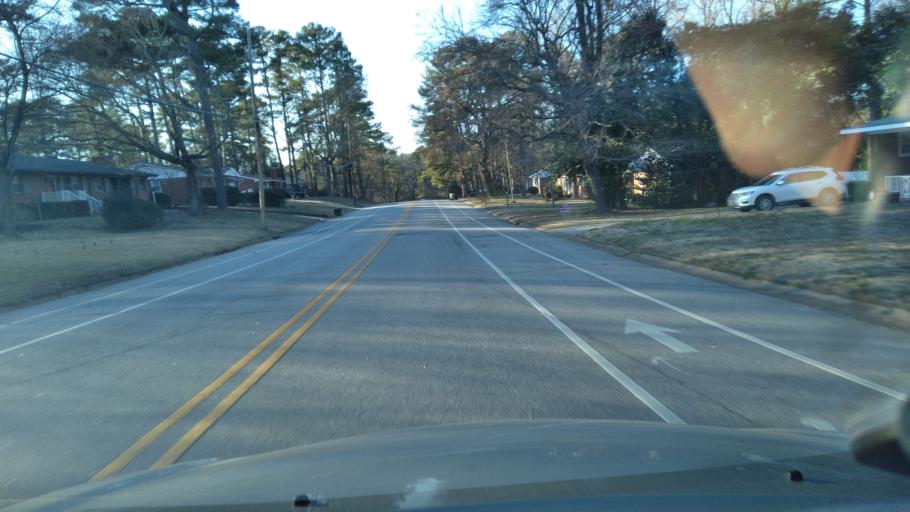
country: US
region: North Carolina
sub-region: Wake County
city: Garner
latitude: 35.6997
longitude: -78.6228
